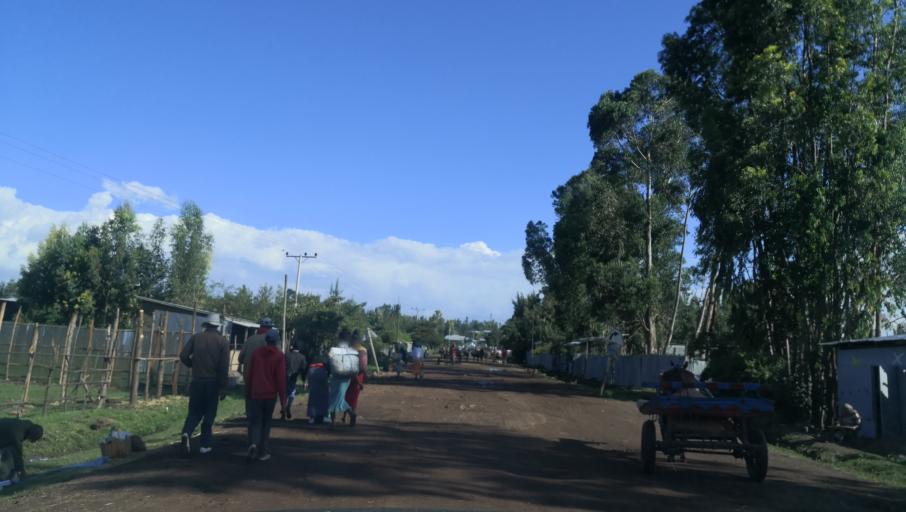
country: ET
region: Oromiya
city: Tulu Bolo
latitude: 8.6554
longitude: 38.2182
